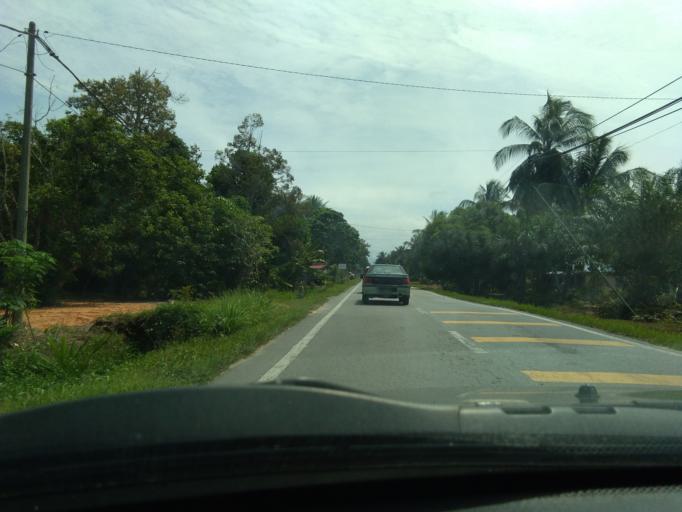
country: MY
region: Perak
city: Bagan Serai
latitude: 5.0465
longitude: 100.5812
